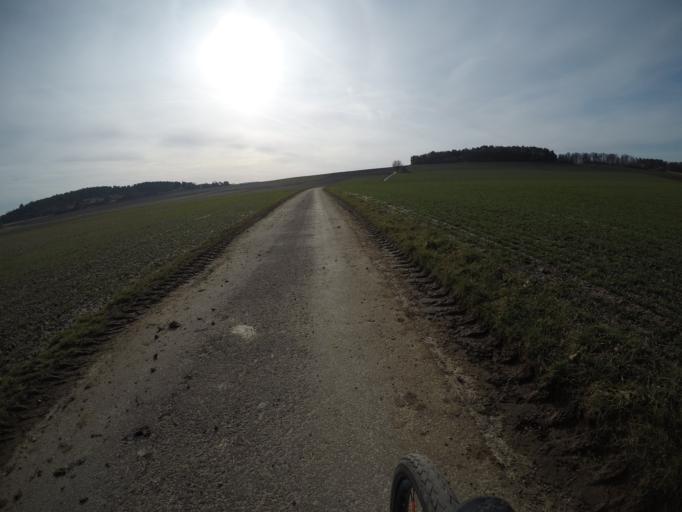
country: DE
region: Baden-Wuerttemberg
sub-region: Karlsruhe Region
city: Ostelsheim
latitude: 48.7012
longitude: 8.8690
